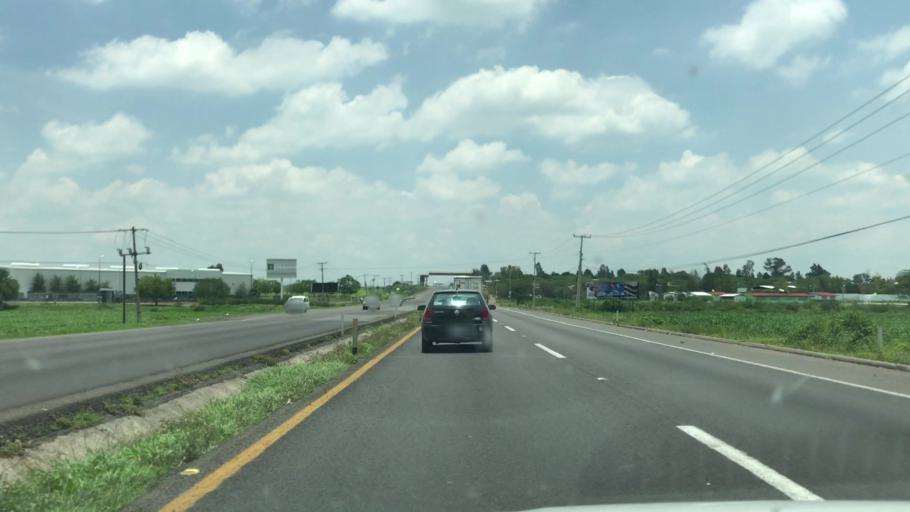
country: MX
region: Guanajuato
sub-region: Irapuato
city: Colonia Morelos de Guadalupe de Rivera
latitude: 20.5775
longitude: -101.4370
